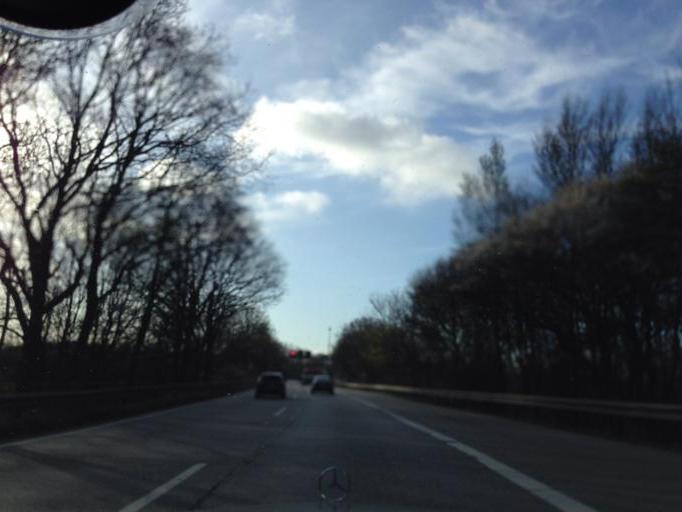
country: DE
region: Hamburg
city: Rothenburgsort
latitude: 53.5044
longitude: 10.0356
